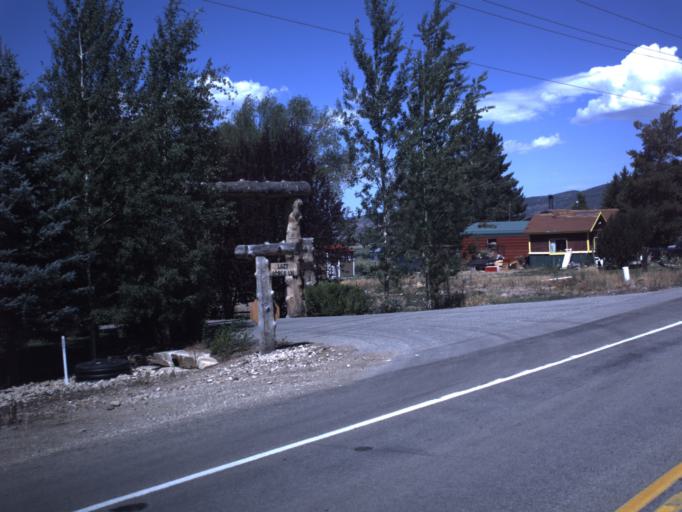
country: US
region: Utah
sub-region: Summit County
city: Oakley
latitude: 40.6843
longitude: -111.2810
